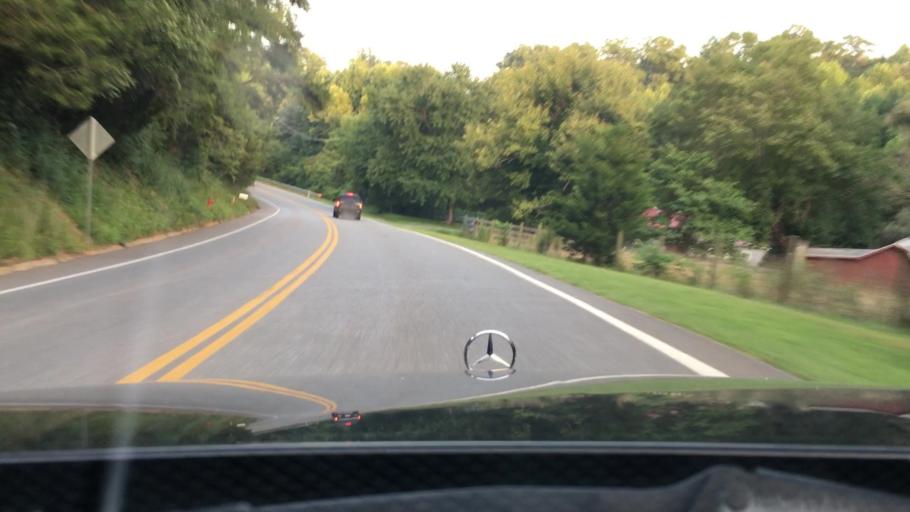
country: US
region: Virginia
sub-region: Campbell County
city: Altavista
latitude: 37.1294
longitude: -79.2789
